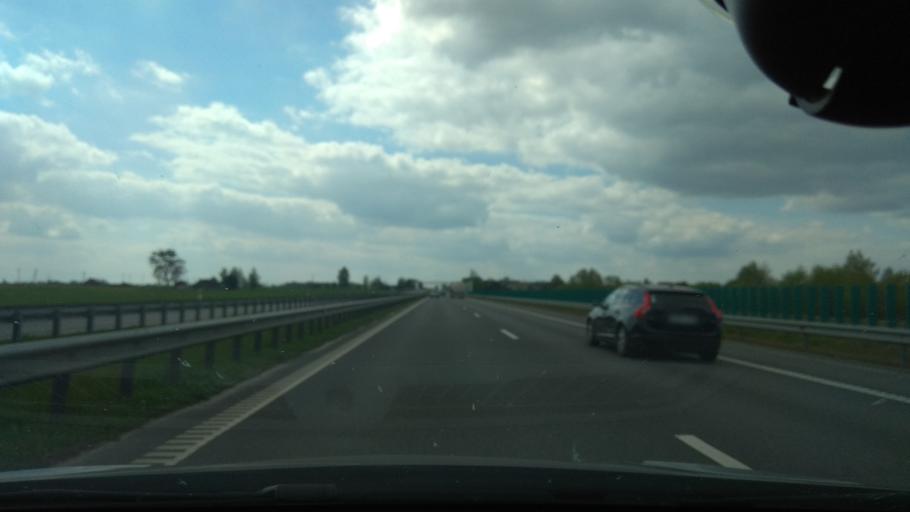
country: LT
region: Kauno apskritis
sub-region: Kauno rajonas
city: Mastaiciai
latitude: 54.7964
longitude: 23.8163
